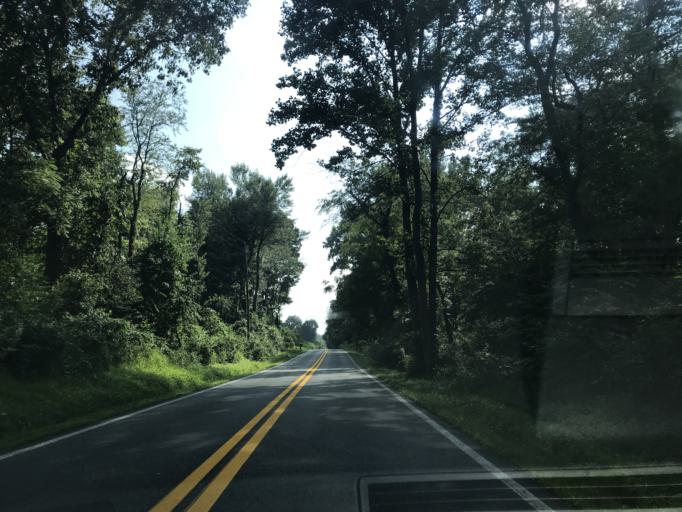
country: US
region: Maryland
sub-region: Carroll County
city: Manchester
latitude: 39.6654
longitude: -76.9085
